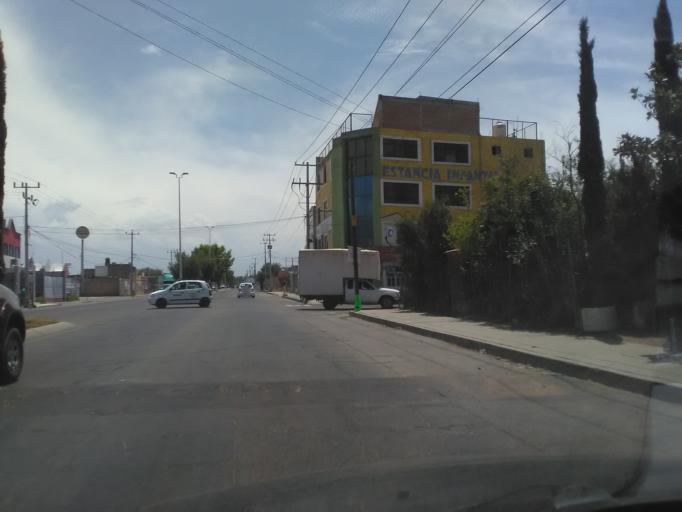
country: MX
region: Durango
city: Victoria de Durango
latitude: 24.0246
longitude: -104.6198
